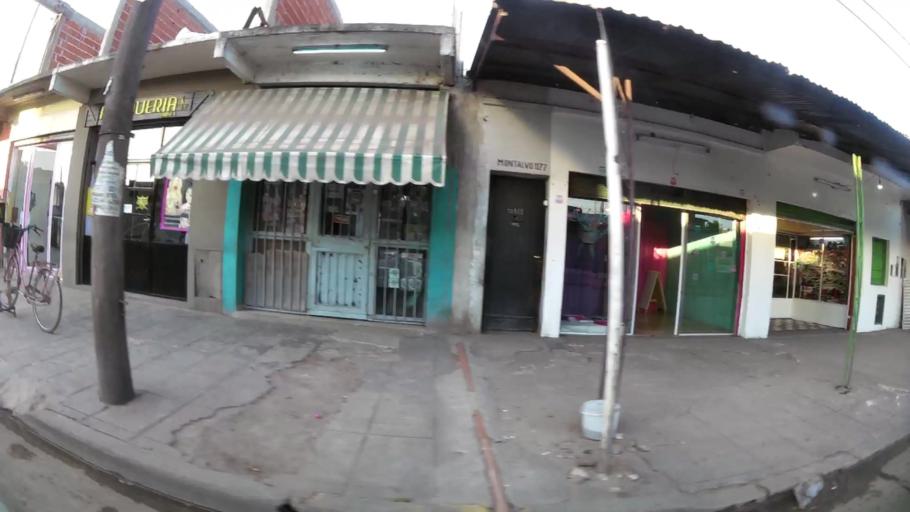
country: AR
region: Buenos Aires
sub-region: Partido de Merlo
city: Merlo
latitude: -34.6720
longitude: -58.7701
